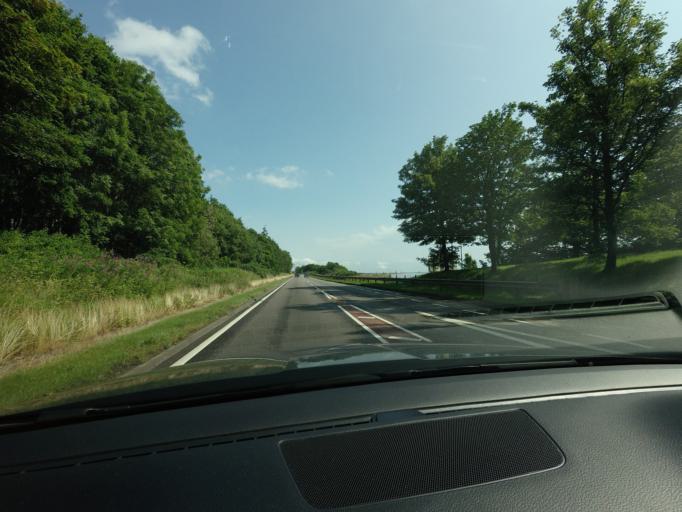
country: GB
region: Scotland
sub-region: Highland
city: Evanton
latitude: 57.6412
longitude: -4.3484
